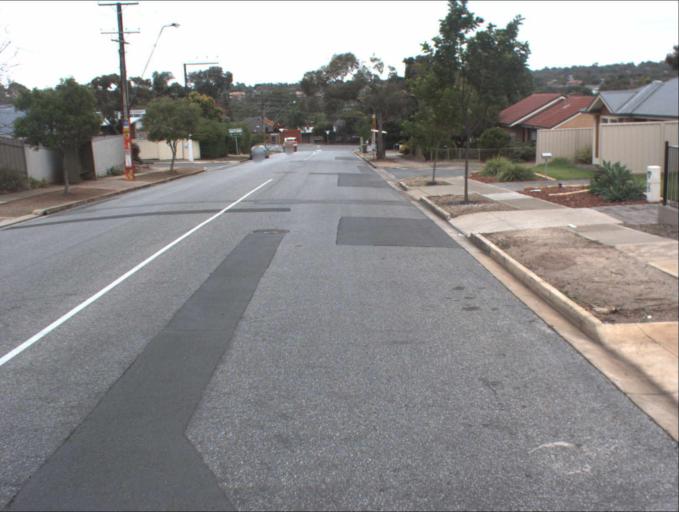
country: AU
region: South Australia
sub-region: Port Adelaide Enfield
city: Gilles Plains
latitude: -34.8470
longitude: 138.6598
